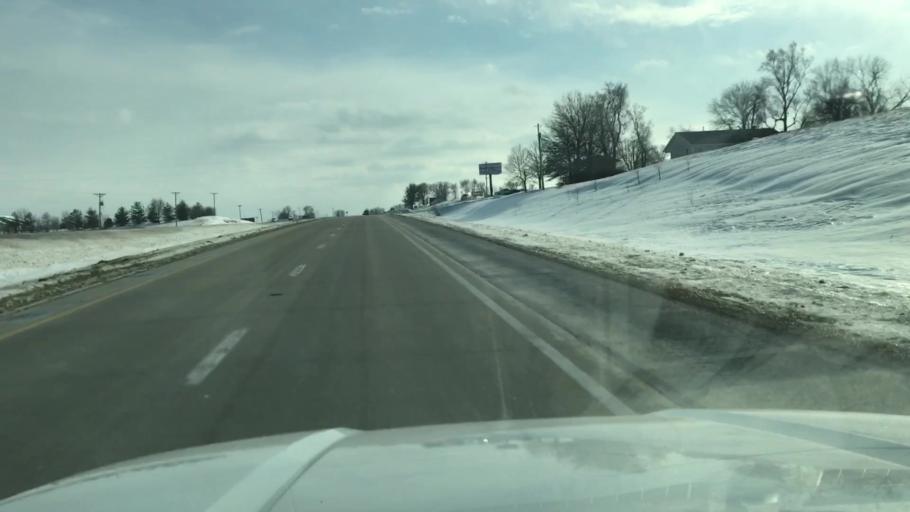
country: US
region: Missouri
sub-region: Nodaway County
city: Maryville
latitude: 40.2928
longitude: -94.8755
